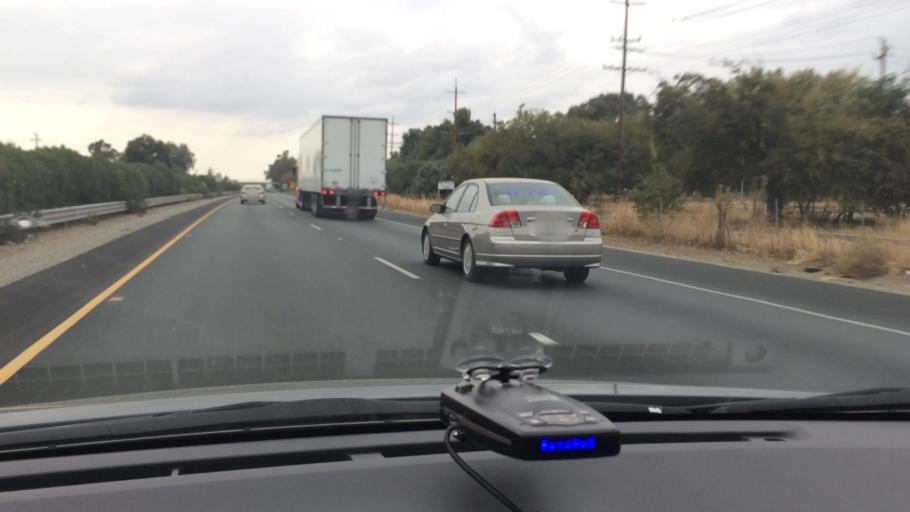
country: US
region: California
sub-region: San Joaquin County
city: Lodi
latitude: 38.1545
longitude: -121.2615
